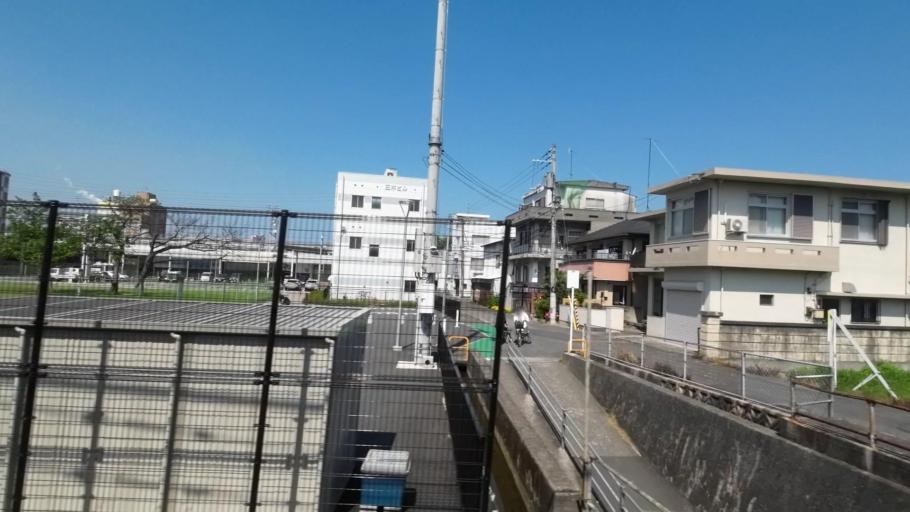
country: JP
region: Ehime
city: Kawanoecho
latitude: 34.0128
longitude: 133.5757
